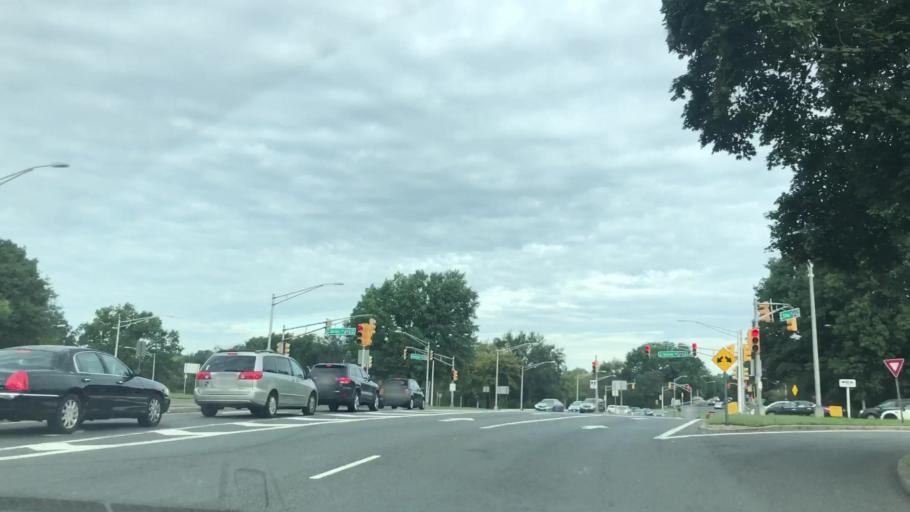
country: US
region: New Jersey
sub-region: Union County
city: Winfield
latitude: 40.6395
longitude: -74.2874
